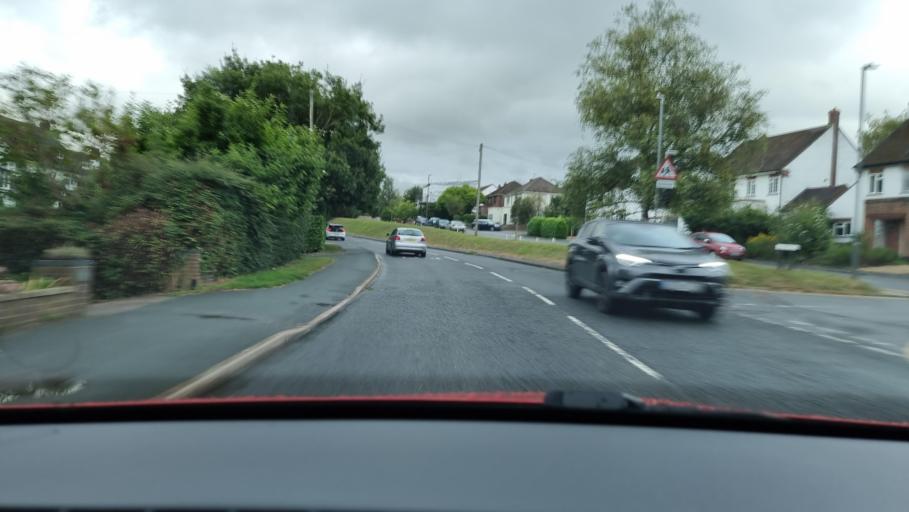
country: GB
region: England
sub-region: Buckinghamshire
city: Chesham
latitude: 51.7086
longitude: -0.6037
